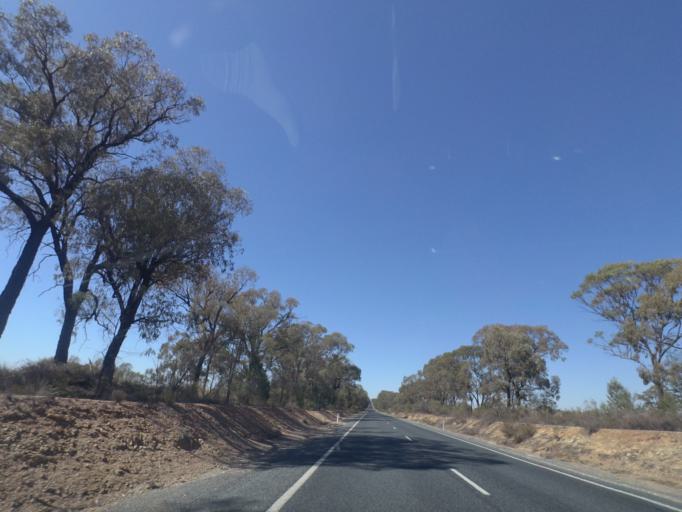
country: AU
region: New South Wales
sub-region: Bland
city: West Wyalong
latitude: -34.1449
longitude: 147.1195
